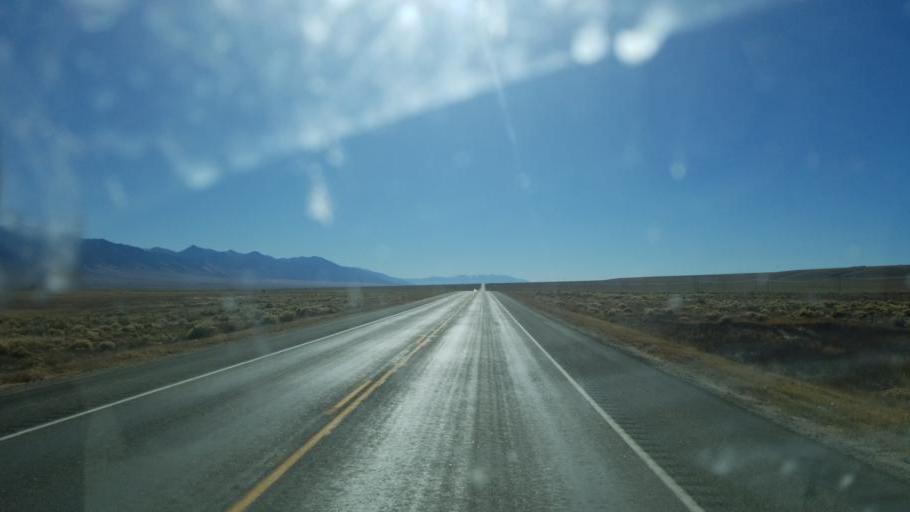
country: US
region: Colorado
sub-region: Chaffee County
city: Salida
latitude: 38.3181
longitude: -106.0017
